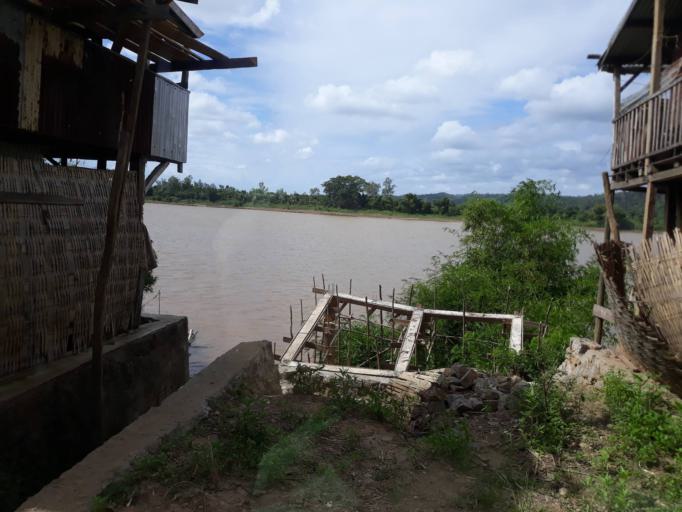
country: MG
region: Atsinanana
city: Ampasimanolotra
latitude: -18.8170
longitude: 49.0700
